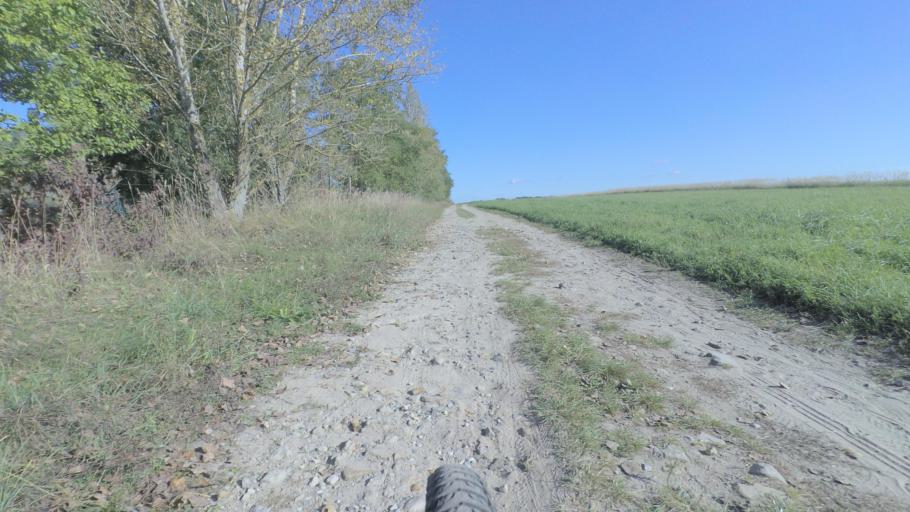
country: DE
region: Brandenburg
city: Rangsdorf
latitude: 52.2736
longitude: 13.4270
